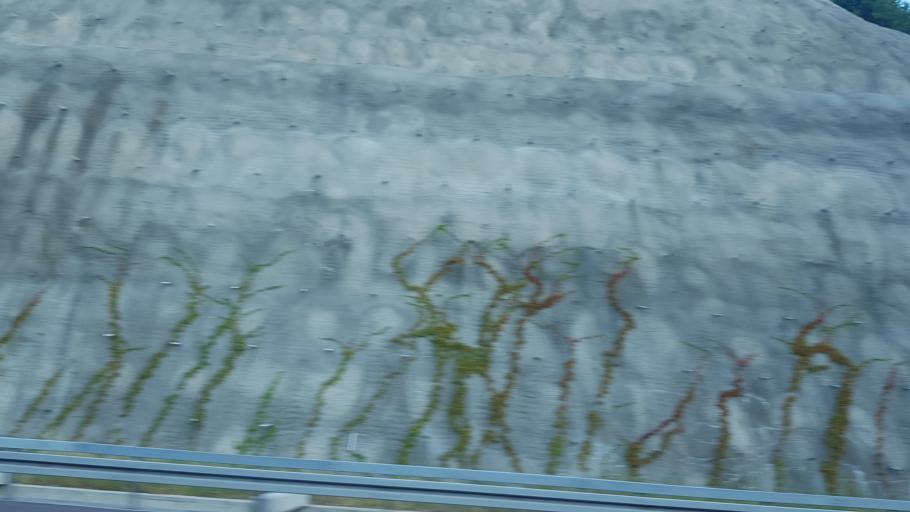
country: TR
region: Bursa
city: Yenikoy
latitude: 40.5855
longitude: 29.3633
